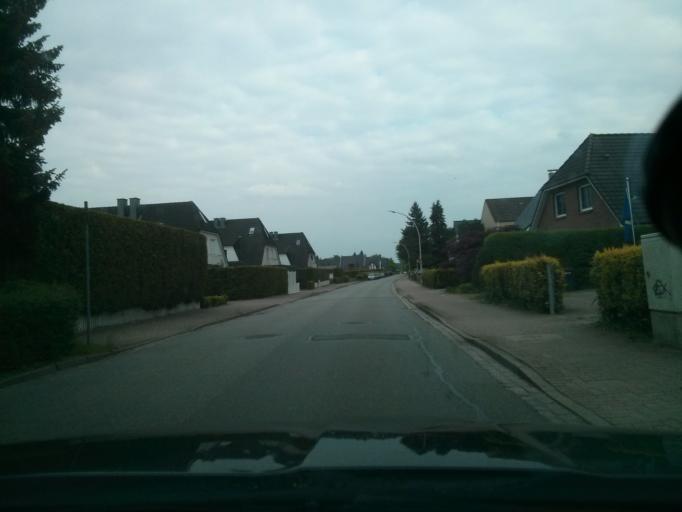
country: DE
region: Schleswig-Holstein
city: Halstenbek
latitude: 53.6360
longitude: 9.8450
